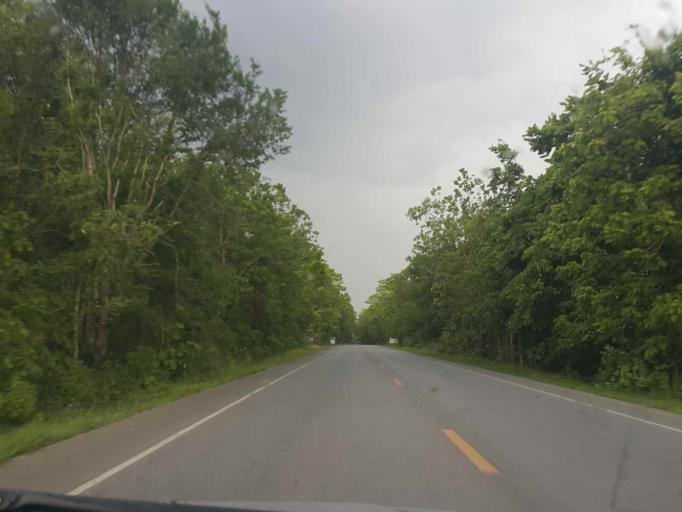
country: TH
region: Phrae
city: Den Chai
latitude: 17.9748
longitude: 100.0096
